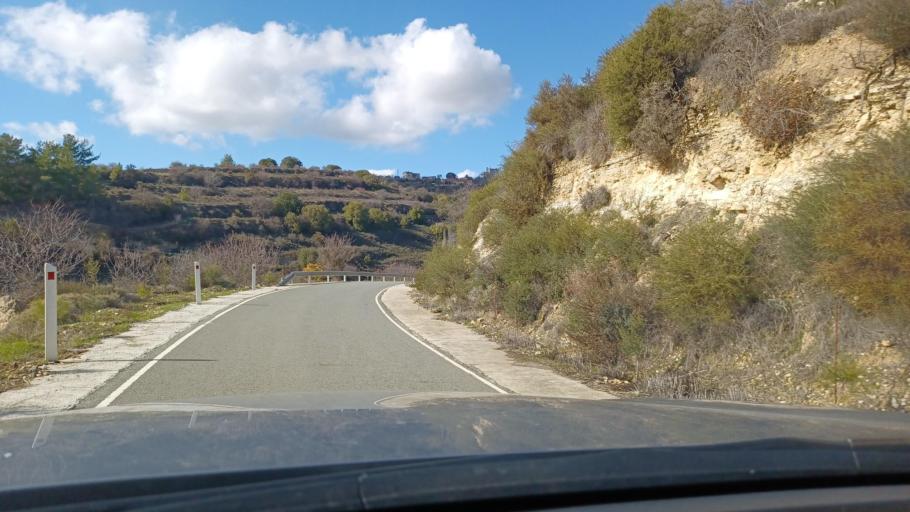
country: CY
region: Limassol
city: Pachna
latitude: 34.8200
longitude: 32.8026
